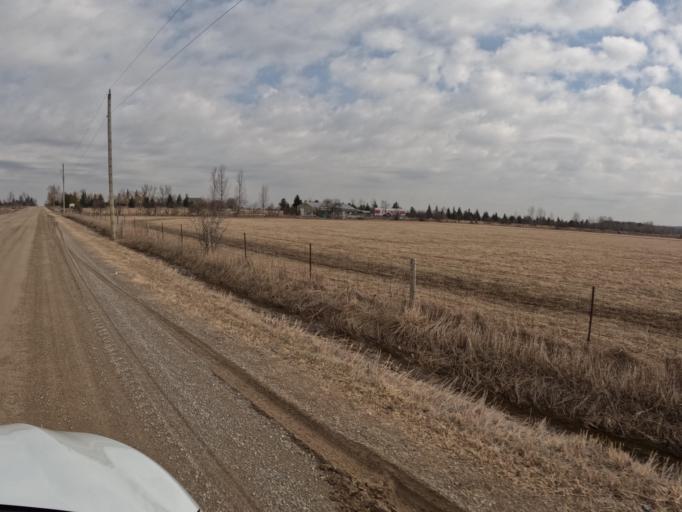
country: CA
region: Ontario
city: Orangeville
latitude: 43.9043
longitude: -80.2141
